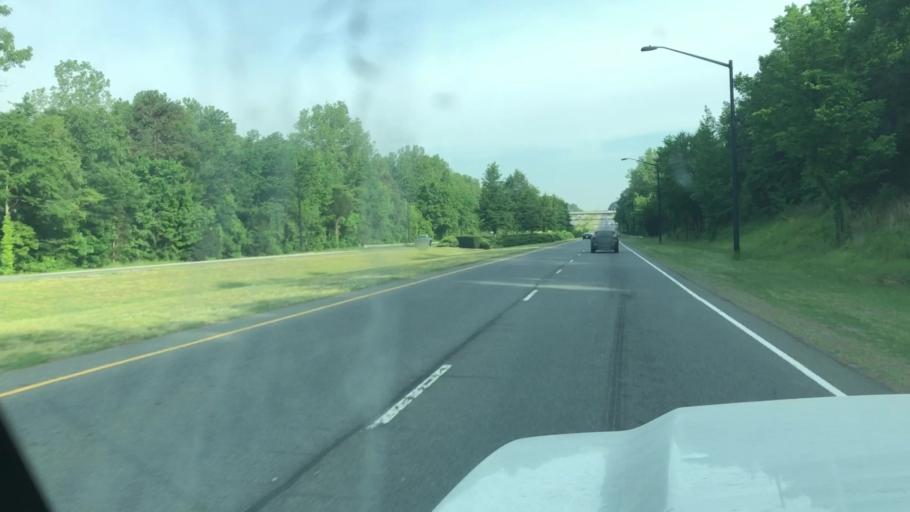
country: US
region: North Carolina
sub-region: Gaston County
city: Mount Holly
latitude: 35.3163
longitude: -80.9335
